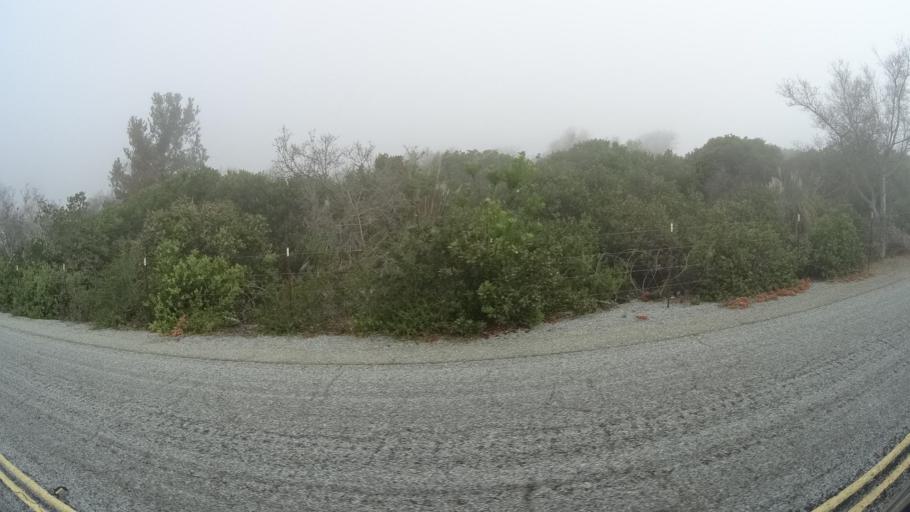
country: US
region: California
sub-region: Monterey County
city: Del Rey Oaks
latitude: 36.5778
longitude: -121.7982
